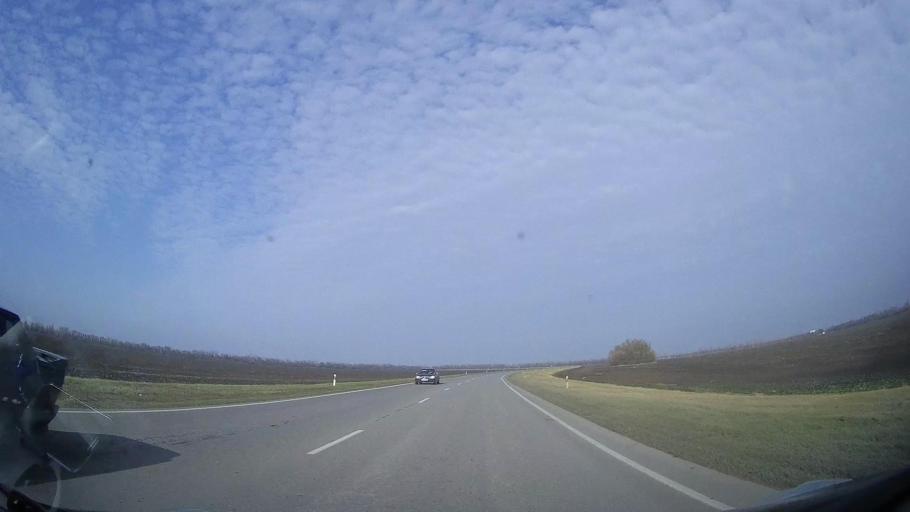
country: RU
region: Rostov
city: Tselina
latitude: 46.5181
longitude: 40.9943
